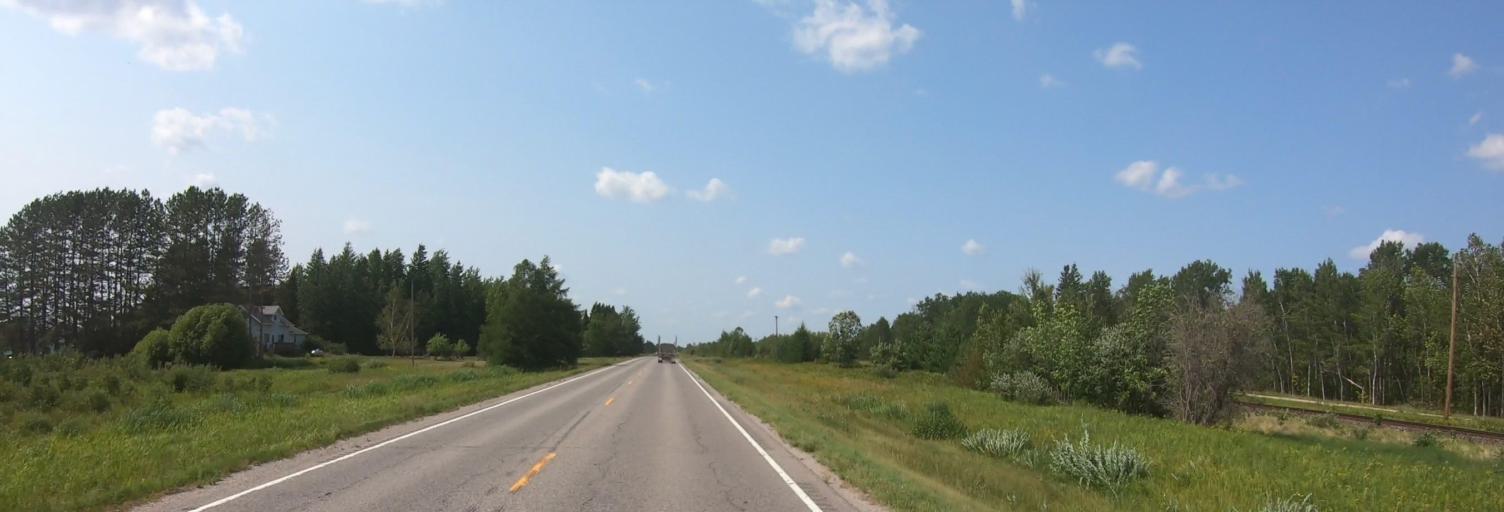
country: US
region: Minnesota
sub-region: Roseau County
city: Warroad
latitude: 48.8177
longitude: -95.1349
